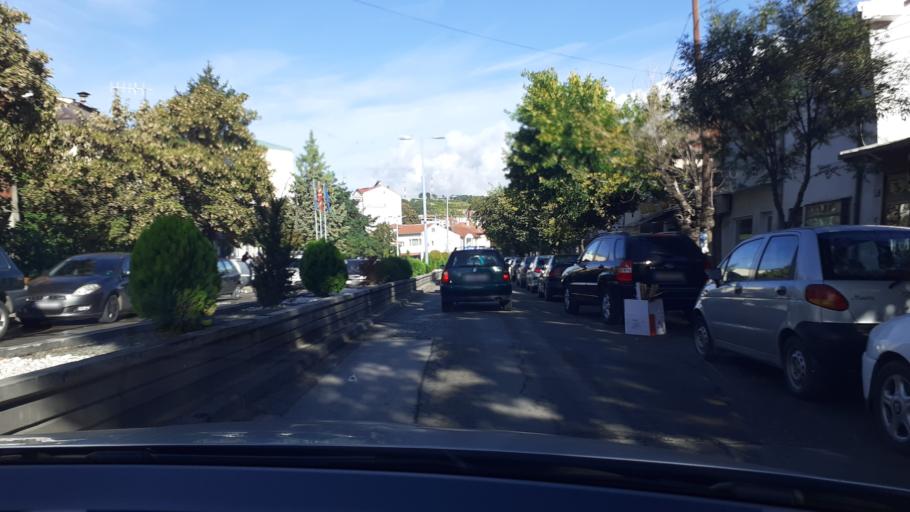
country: MK
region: Kocani
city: Kochani
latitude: 41.9140
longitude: 22.4145
